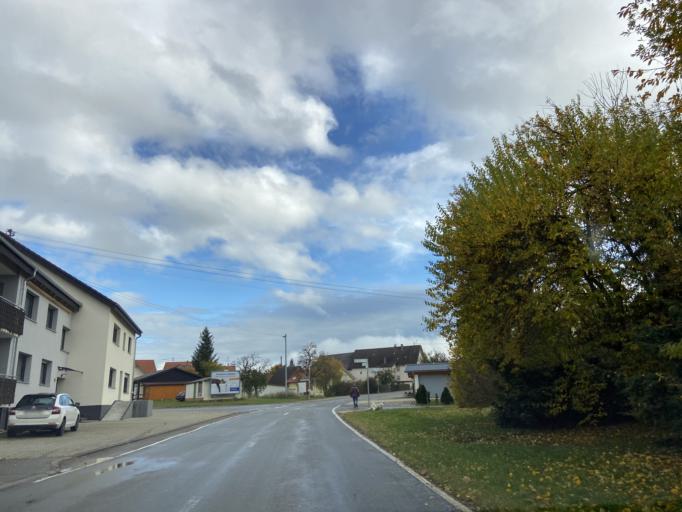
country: DE
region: Baden-Wuerttemberg
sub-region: Tuebingen Region
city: Leibertingen
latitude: 48.0560
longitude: 9.0509
